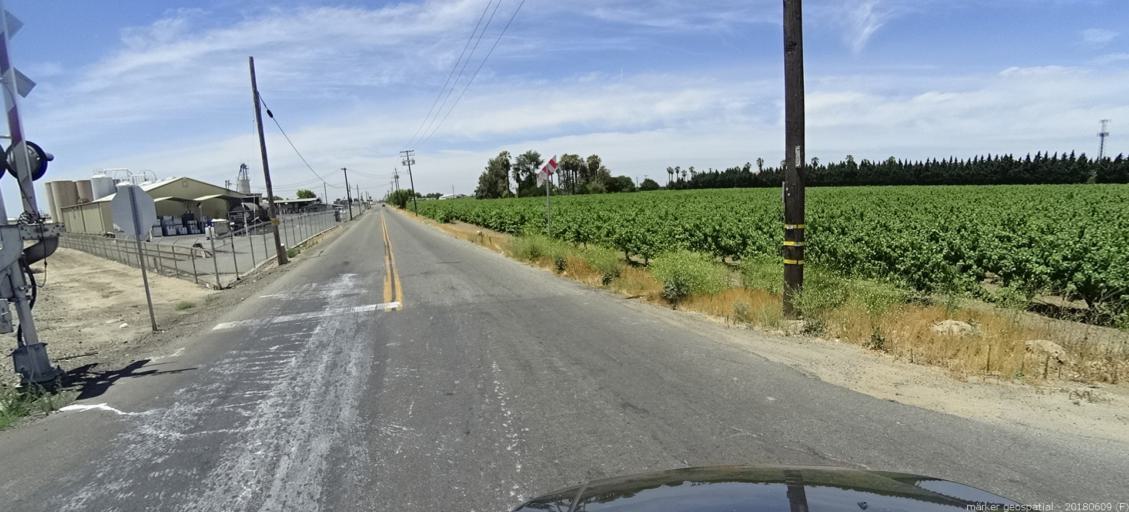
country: US
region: California
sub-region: Madera County
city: Madera
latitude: 36.9383
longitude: -120.0921
